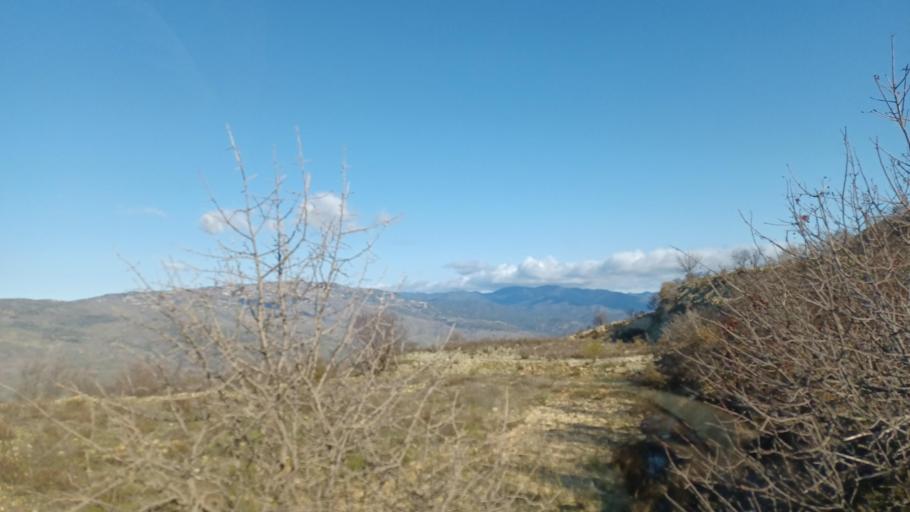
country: CY
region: Limassol
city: Pachna
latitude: 34.8112
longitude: 32.6636
